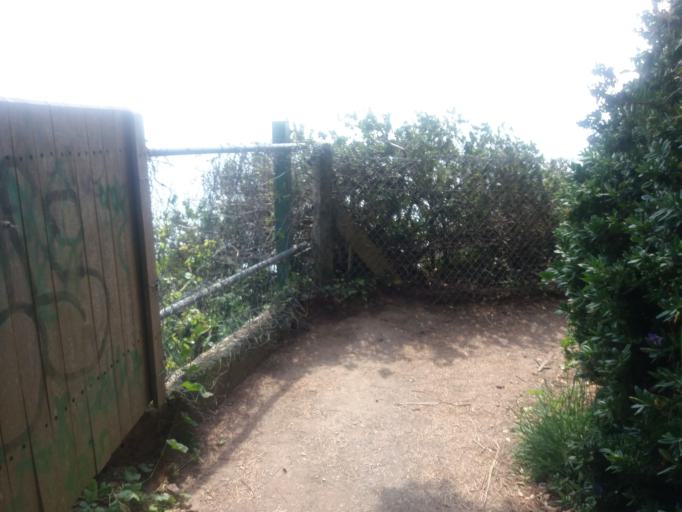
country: IE
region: Leinster
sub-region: Fingal County
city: Howth
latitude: 53.3639
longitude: -6.0613
